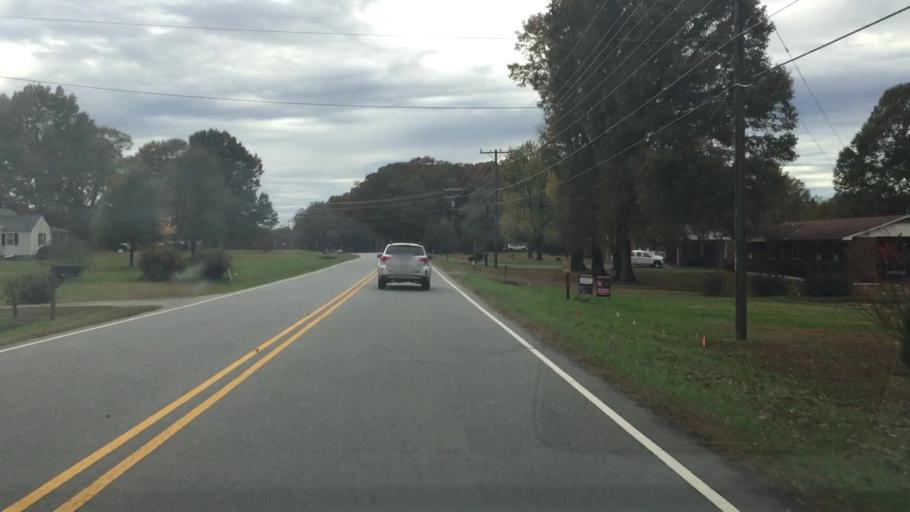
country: US
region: North Carolina
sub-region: Rockingham County
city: Wentworth
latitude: 36.2746
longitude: -79.7829
